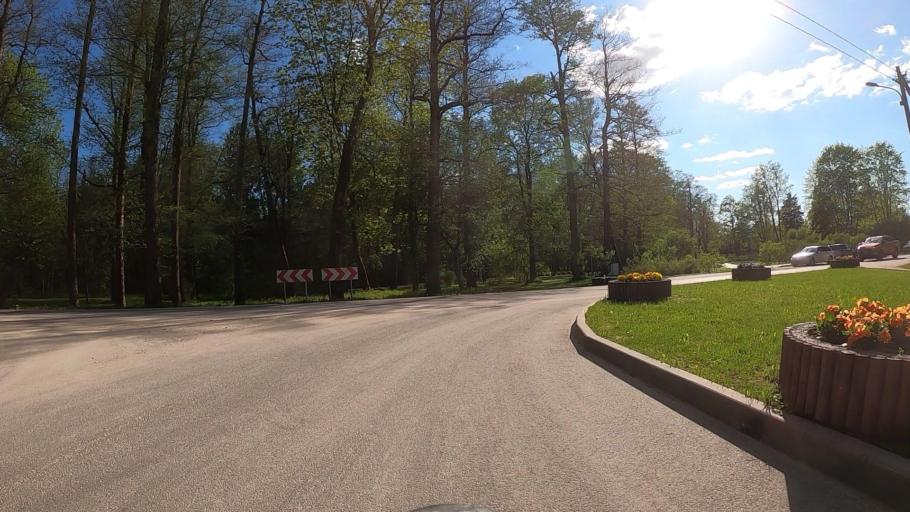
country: LV
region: Baldone
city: Baldone
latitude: 56.7432
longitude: 24.4062
